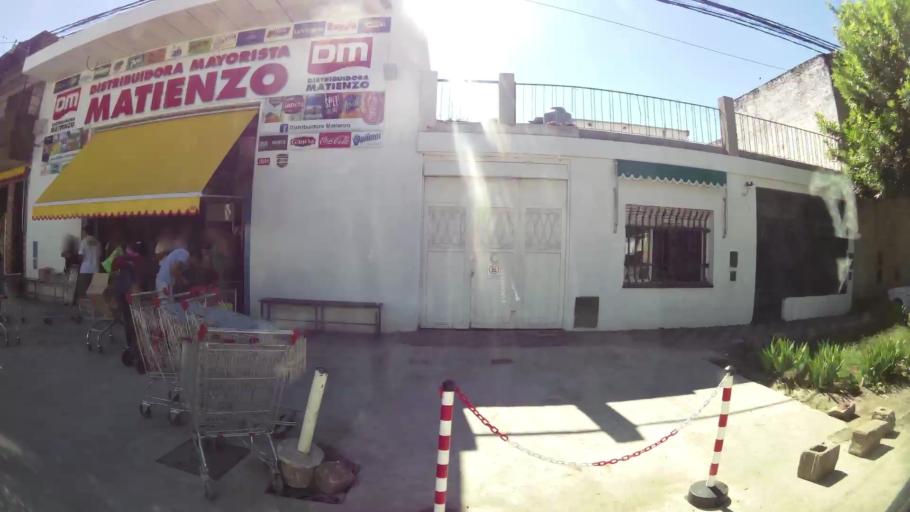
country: AR
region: Santa Fe
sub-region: Departamento de Rosario
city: Rosario
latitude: -32.9598
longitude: -60.6939
